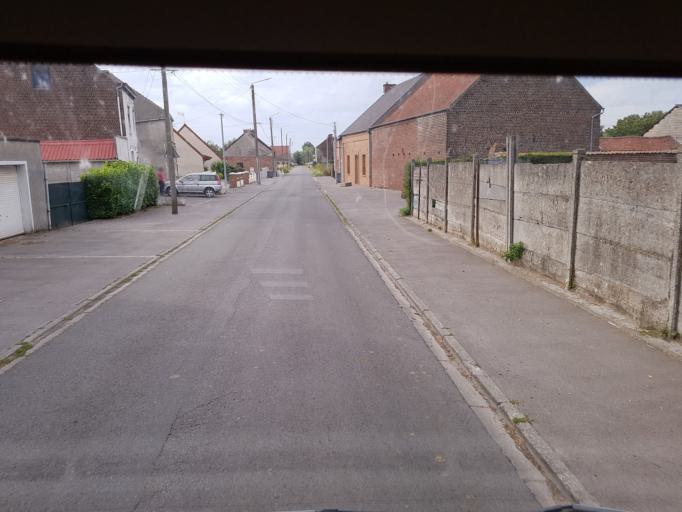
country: FR
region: Nord-Pas-de-Calais
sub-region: Departement du Nord
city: Vieux-Conde
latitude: 50.4793
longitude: 3.5667
